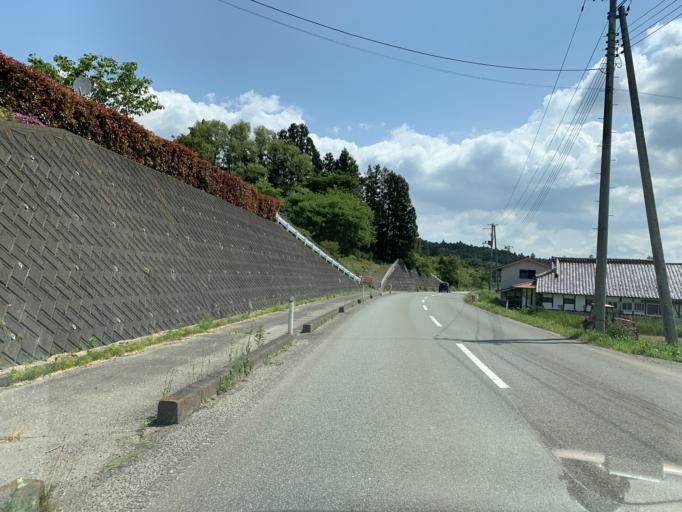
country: JP
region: Miyagi
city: Furukawa
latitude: 38.6855
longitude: 140.9657
